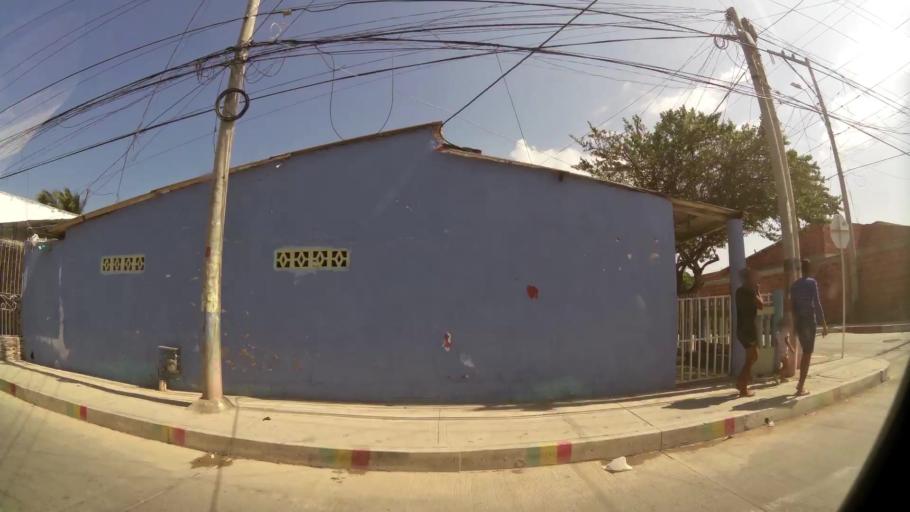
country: CO
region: Atlantico
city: Barranquilla
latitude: 10.9708
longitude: -74.8362
